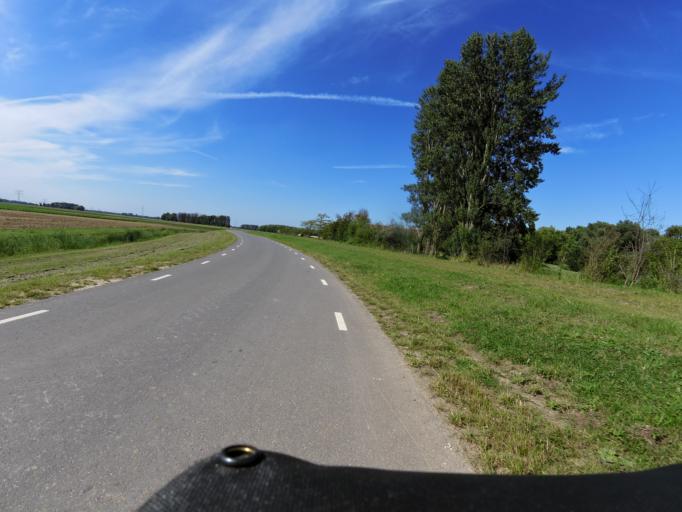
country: NL
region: North Brabant
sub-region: Gemeente Werkendam
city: Werkendam
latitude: 51.7705
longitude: 4.8576
